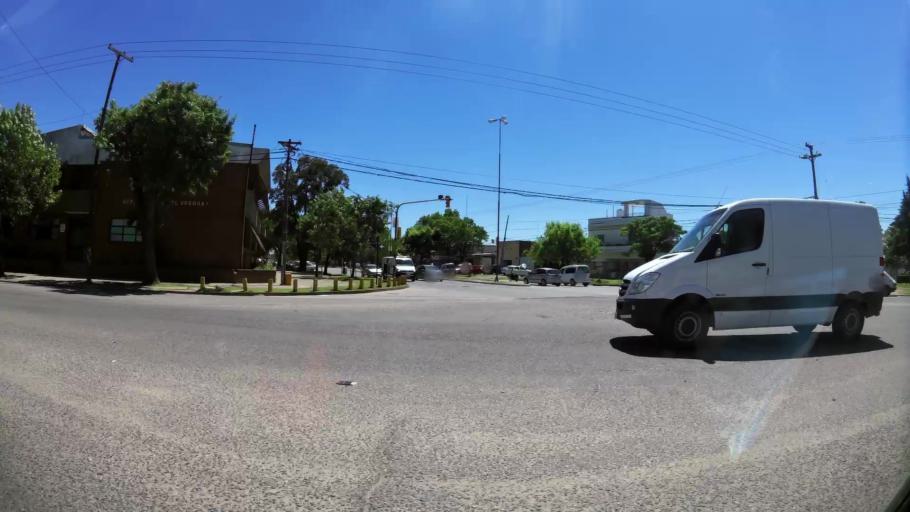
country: AR
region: Santa Fe
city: Santa Fe de la Vera Cruz
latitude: -31.6187
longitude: -60.7136
